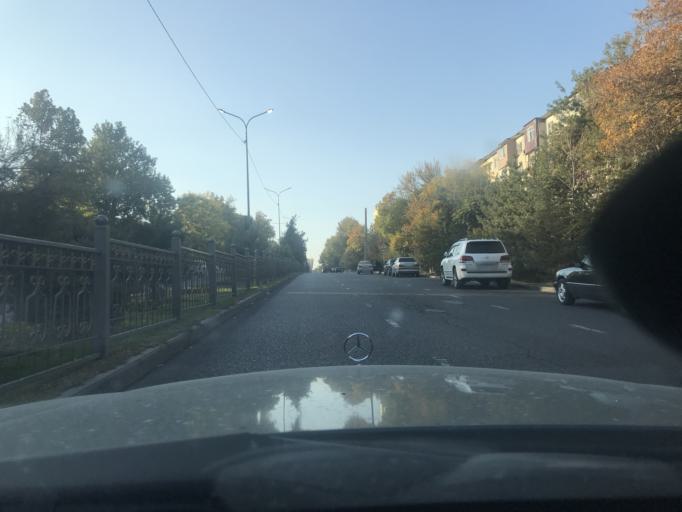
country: KZ
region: Ongtustik Qazaqstan
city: Shymkent
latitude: 42.3021
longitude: 69.6056
